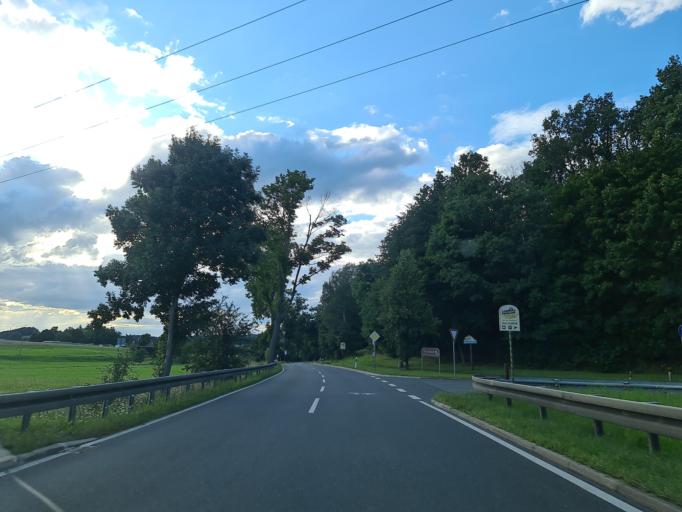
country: DE
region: Saxony
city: Pausa
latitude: 50.5726
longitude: 11.9972
